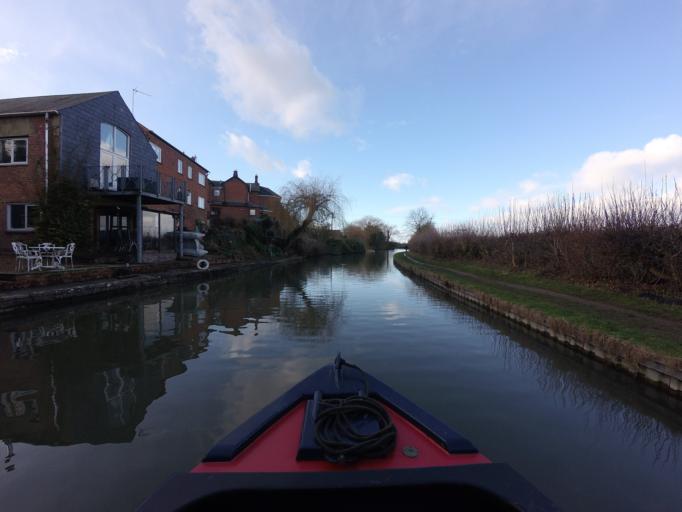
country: GB
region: England
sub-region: Northamptonshire
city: Bugbrooke
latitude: 52.2257
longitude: -1.0585
